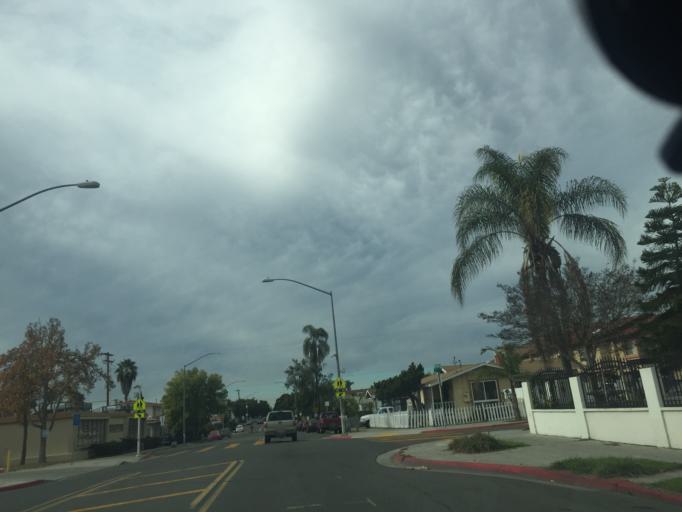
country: US
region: California
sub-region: San Diego County
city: Lemon Grove
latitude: 32.7530
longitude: -117.0930
